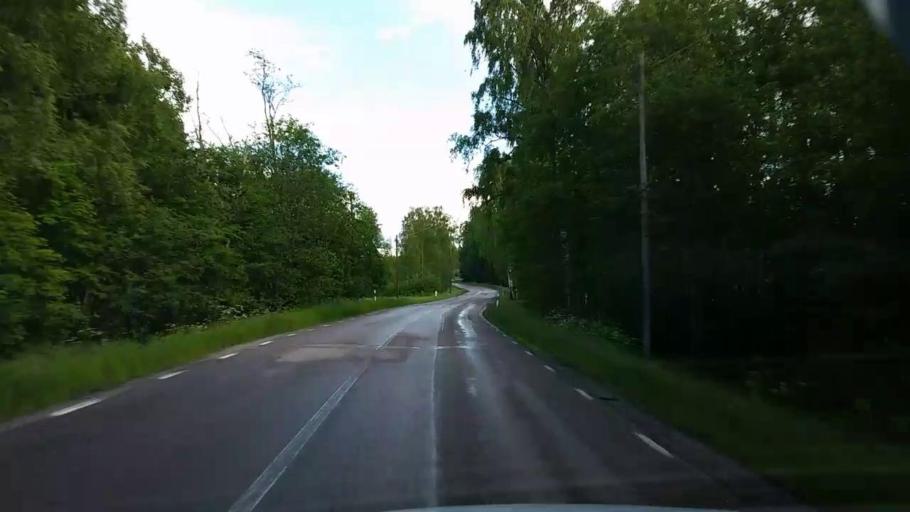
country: SE
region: Vaestmanland
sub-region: Fagersta Kommun
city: Fagersta
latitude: 59.9457
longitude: 15.7993
